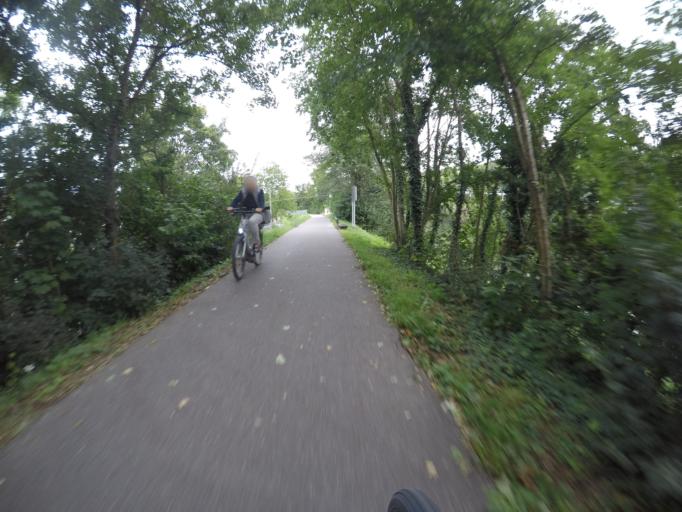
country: DE
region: Baden-Wuerttemberg
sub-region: Regierungsbezirk Stuttgart
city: Stuttgart Muehlhausen
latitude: 48.8780
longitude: 9.2764
